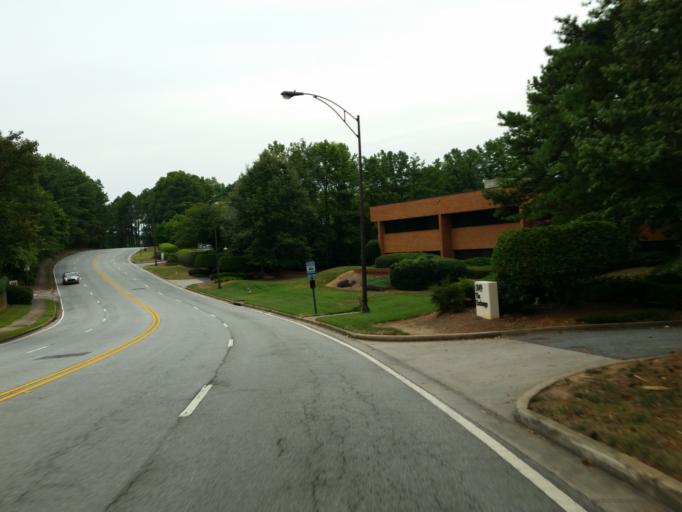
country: US
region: Georgia
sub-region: Cobb County
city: Smyrna
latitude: 33.9070
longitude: -84.4783
